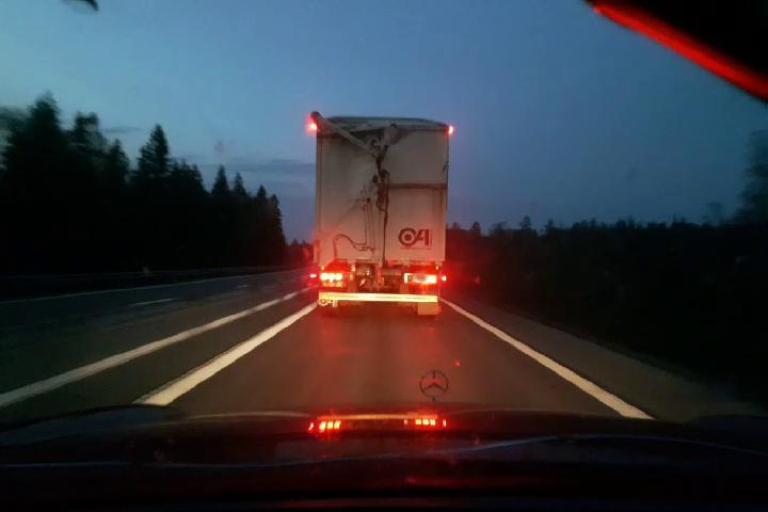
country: SE
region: Vaesternorrland
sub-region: OErnskoeldsviks Kommun
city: Bjasta
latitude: 63.1217
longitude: 18.3978
